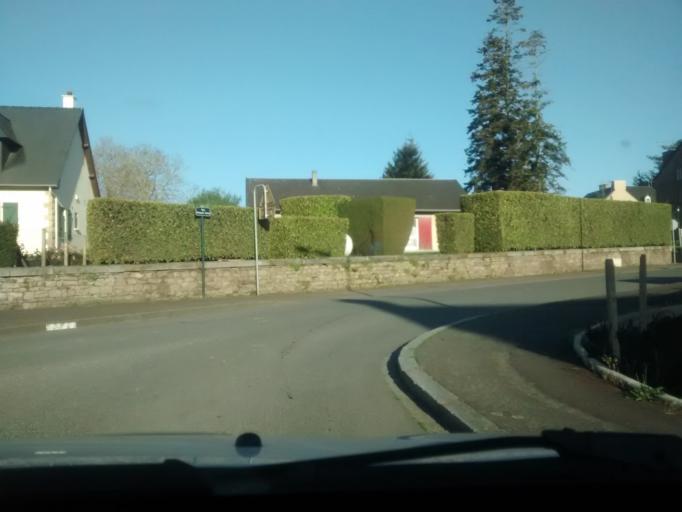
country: FR
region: Brittany
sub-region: Departement d'Ille-et-Vilaine
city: Pleine-Fougeres
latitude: 48.5311
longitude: -1.5654
